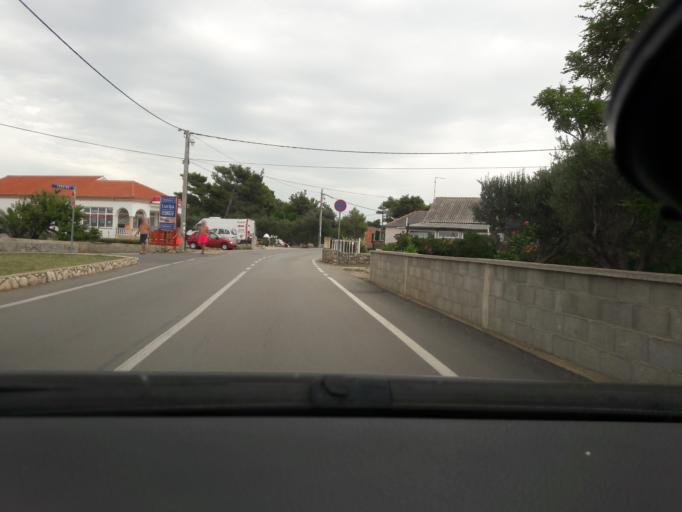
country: HR
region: Zadarska
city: Vir
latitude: 44.3038
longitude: 15.0802
